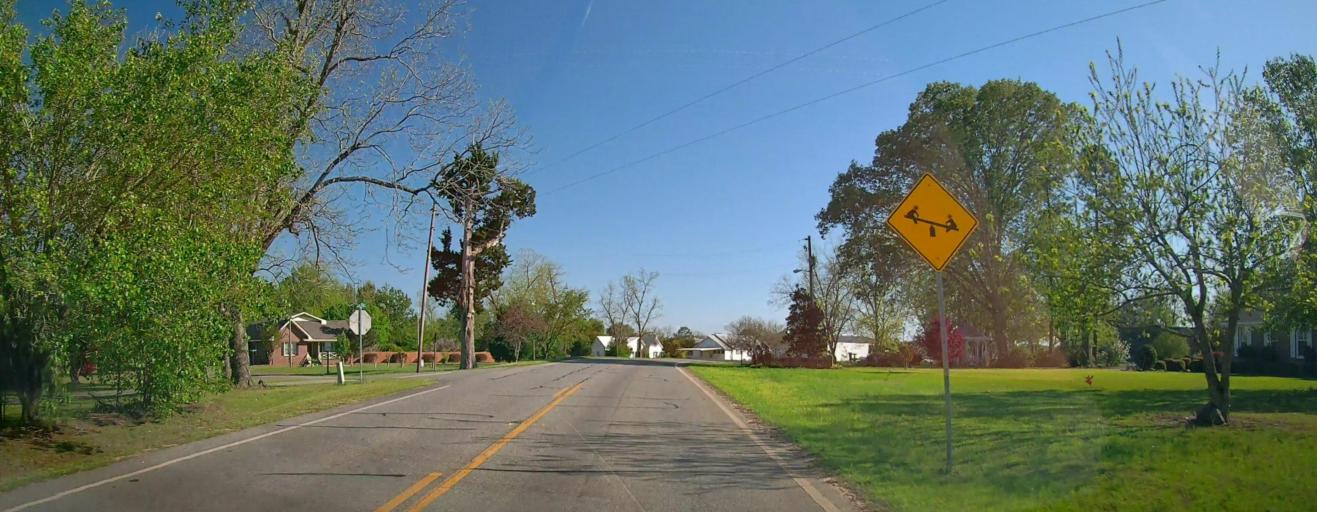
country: US
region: Georgia
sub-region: Wilcox County
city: Rochelle
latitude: 31.8112
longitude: -83.4890
